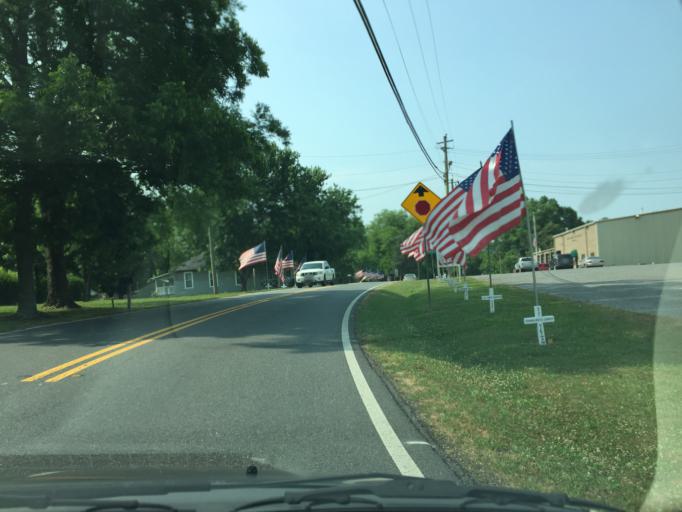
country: US
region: Georgia
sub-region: Catoosa County
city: Ringgold
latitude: 34.9163
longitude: -85.1062
